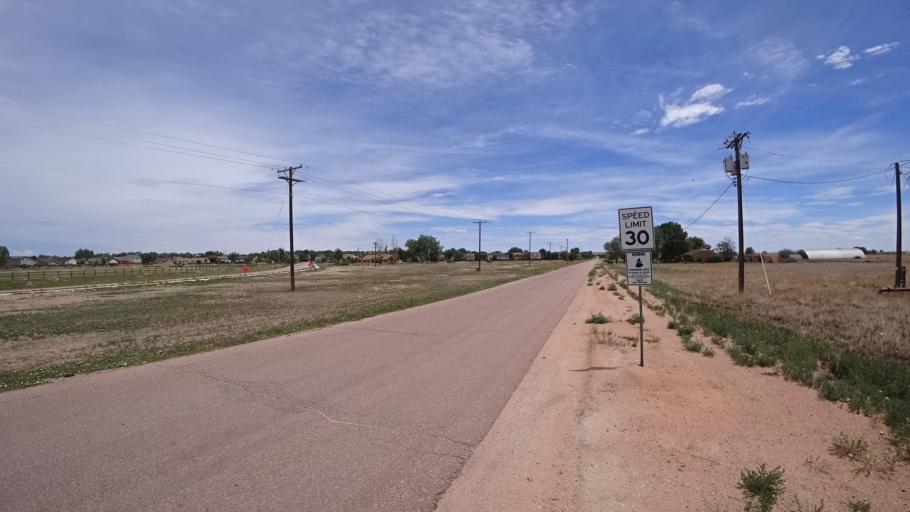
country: US
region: Colorado
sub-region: El Paso County
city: Fountain
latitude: 38.6644
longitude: -104.6843
